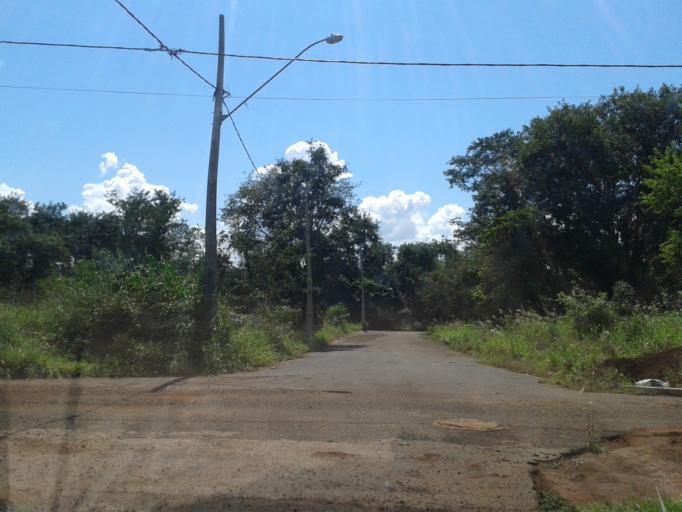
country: BR
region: Goias
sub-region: Itumbiara
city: Itumbiara
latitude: -18.4212
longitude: -49.1850
